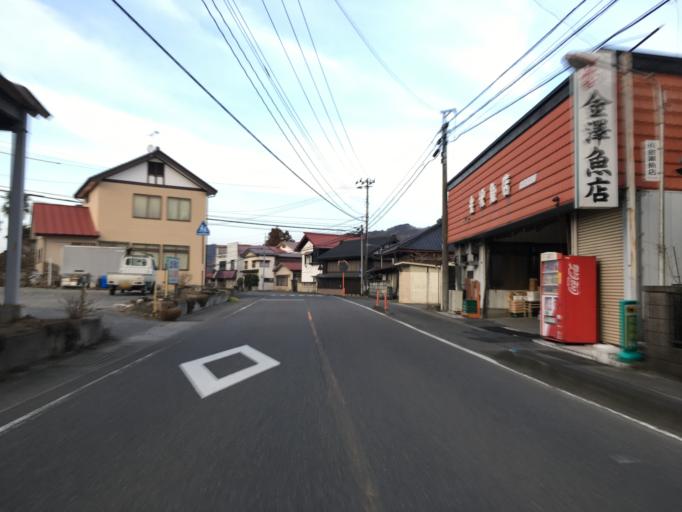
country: JP
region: Ibaraki
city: Daigo
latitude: 36.9047
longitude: 140.4067
